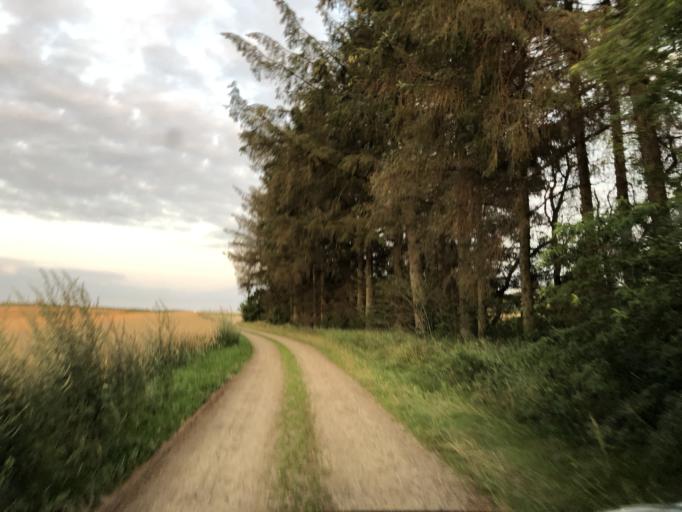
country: DK
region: Central Jutland
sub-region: Holstebro Kommune
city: Vinderup
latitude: 56.4552
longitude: 8.8974
